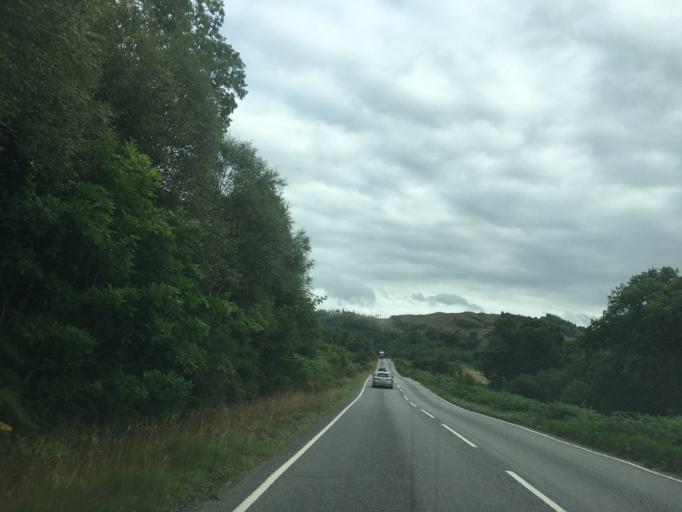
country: GB
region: Scotland
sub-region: Argyll and Bute
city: Oban
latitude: 56.3254
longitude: -5.5011
